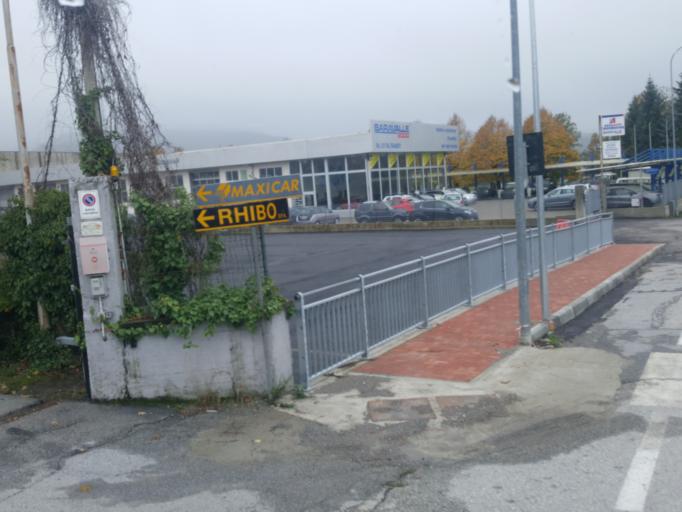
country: IT
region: Piedmont
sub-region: Provincia di Cuneo
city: Ceva
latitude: 44.3769
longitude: 8.0388
